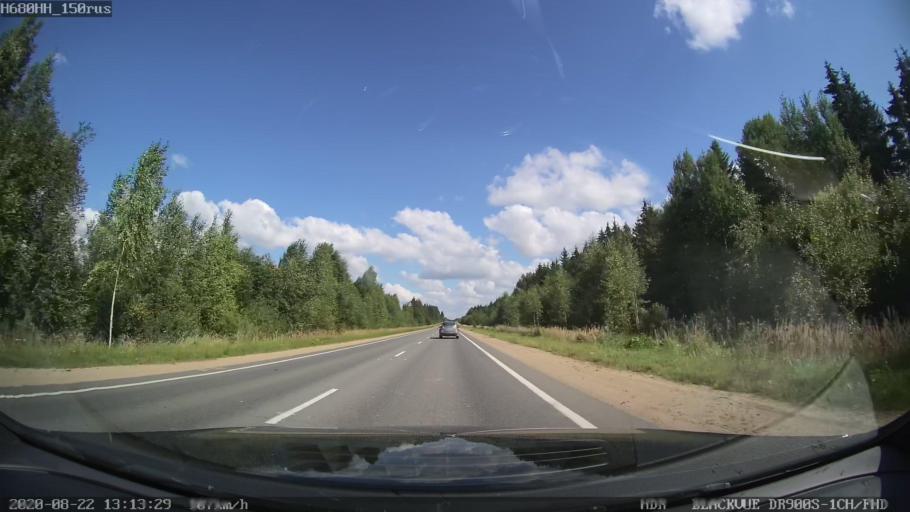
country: RU
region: Tverskaya
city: Bezhetsk
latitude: 57.7505
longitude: 36.5742
